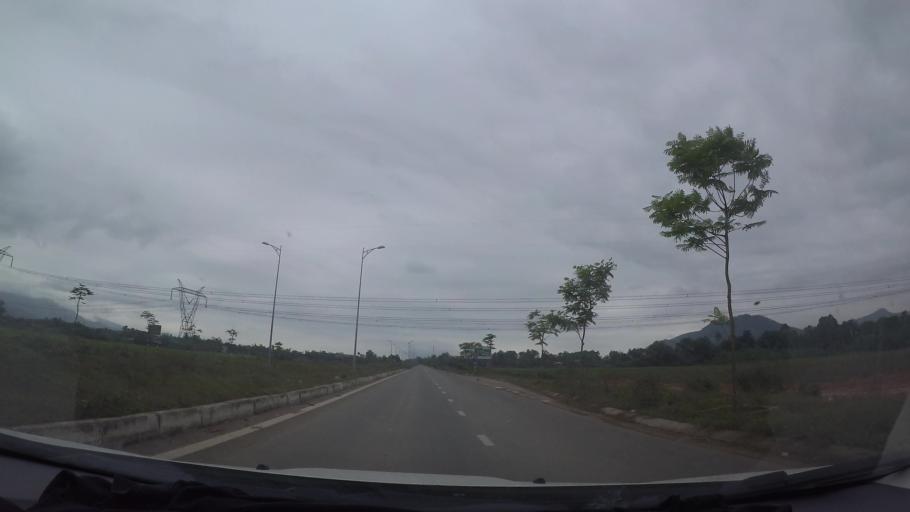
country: VN
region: Da Nang
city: Lien Chieu
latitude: 16.0750
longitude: 108.0895
